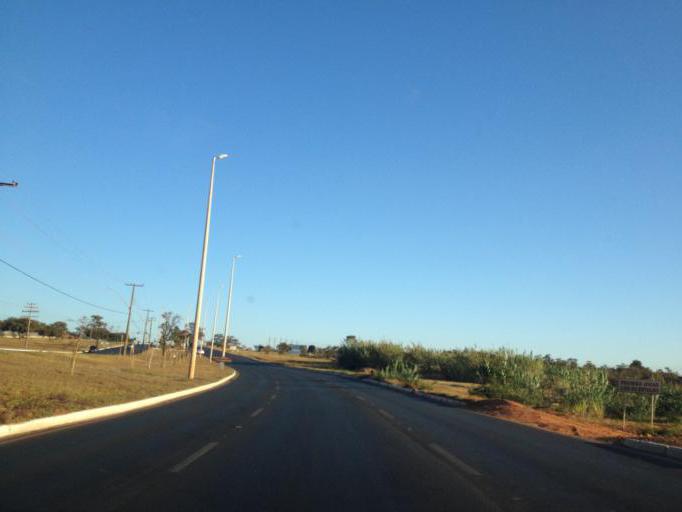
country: BR
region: Federal District
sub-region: Brasilia
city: Brasilia
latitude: -15.7643
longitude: -47.9159
